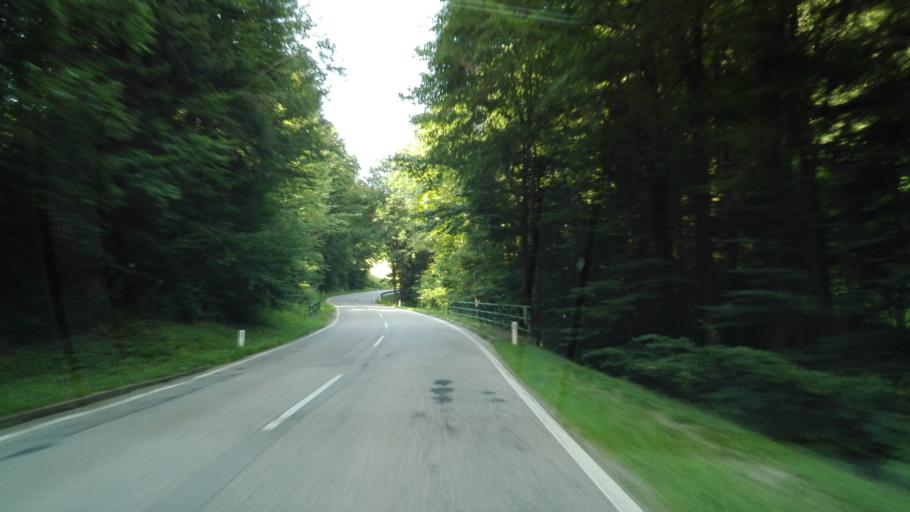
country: AT
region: Lower Austria
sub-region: Politischer Bezirk Lilienfeld
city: Hainfeld
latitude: 48.0839
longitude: 15.7795
